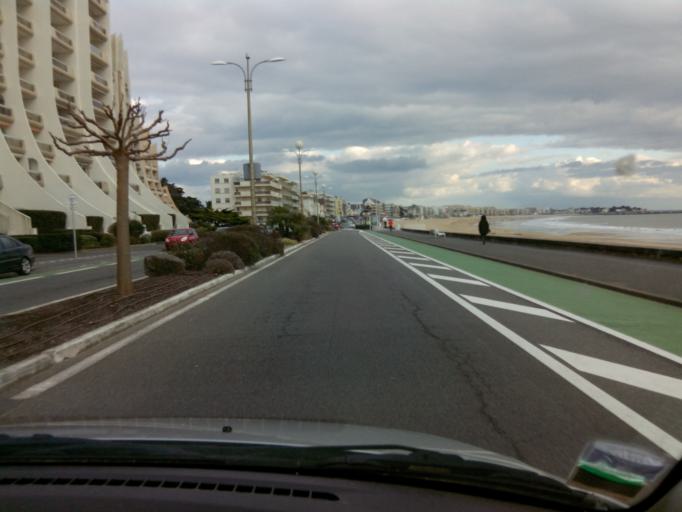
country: FR
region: Pays de la Loire
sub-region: Departement de la Loire-Atlantique
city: La Baule-Escoublac
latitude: 47.2739
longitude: -2.3593
